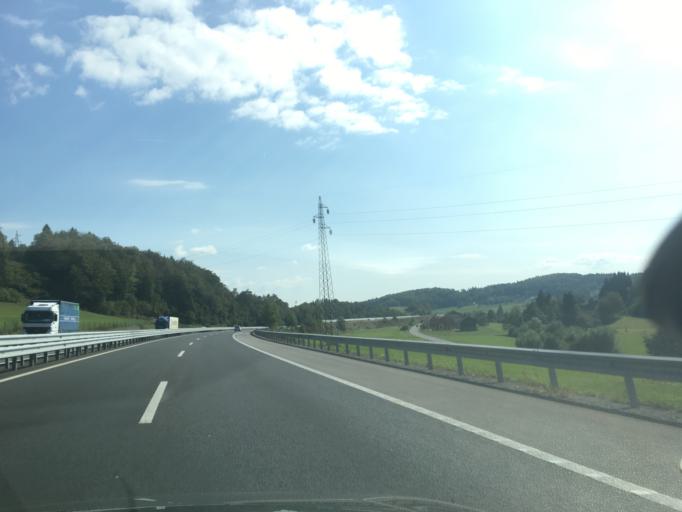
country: SI
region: Ivancna Gorica
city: Ivancna Gorica
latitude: 45.9463
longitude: 14.7754
